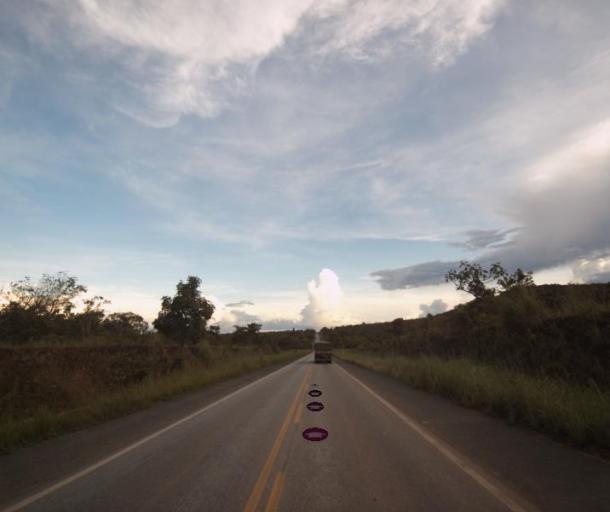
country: BR
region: Goias
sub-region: Uruacu
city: Uruacu
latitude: -14.2131
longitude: -49.1311
